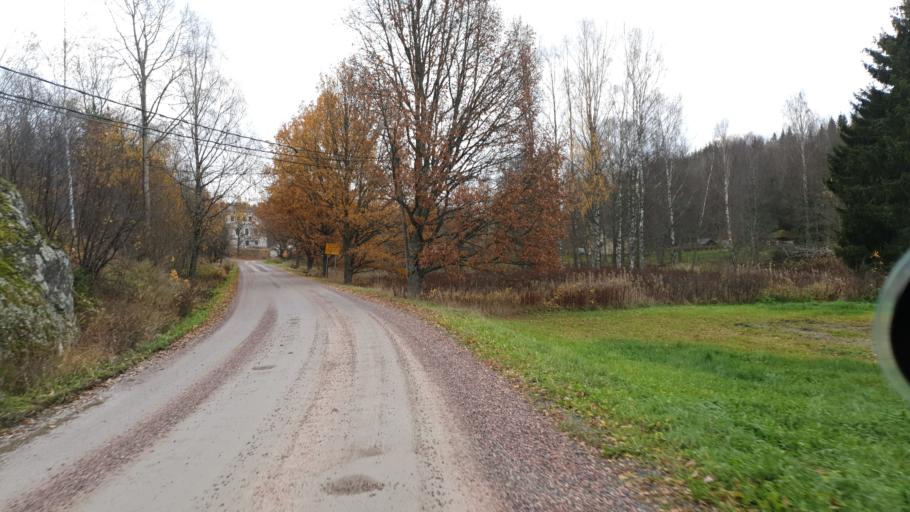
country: FI
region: Uusimaa
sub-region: Helsinki
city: Siuntio
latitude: 60.1430
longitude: 24.2611
